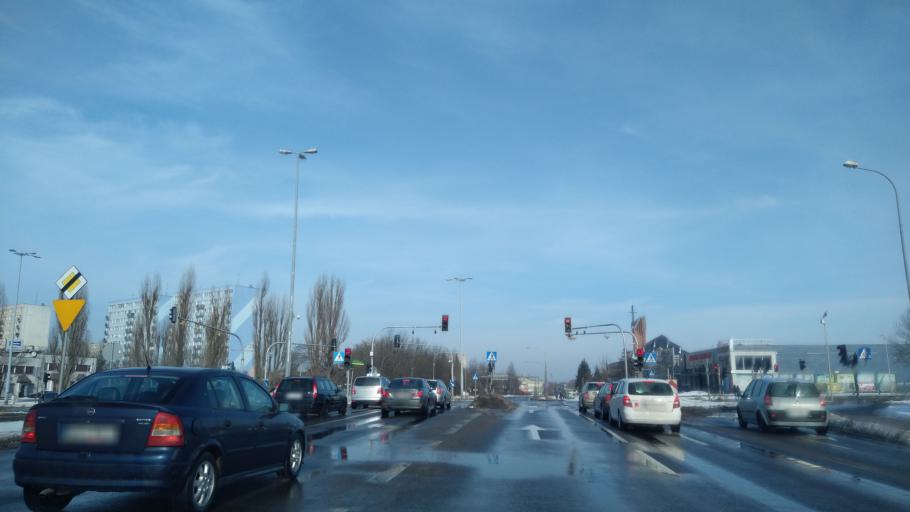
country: PL
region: Warmian-Masurian Voivodeship
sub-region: Powiat olsztynski
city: Olsztyn
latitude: 53.7625
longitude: 20.5007
